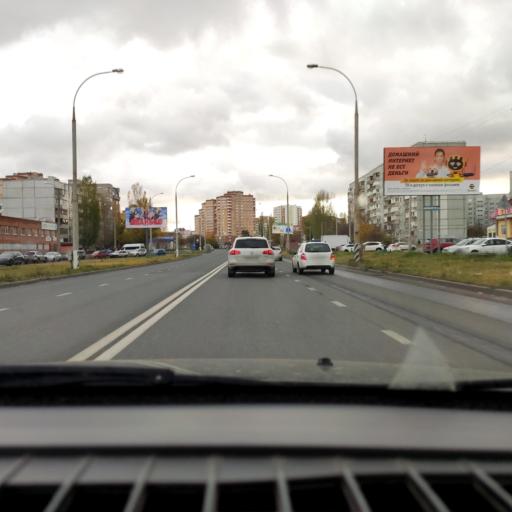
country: RU
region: Samara
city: Tol'yatti
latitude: 53.5431
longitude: 49.3608
